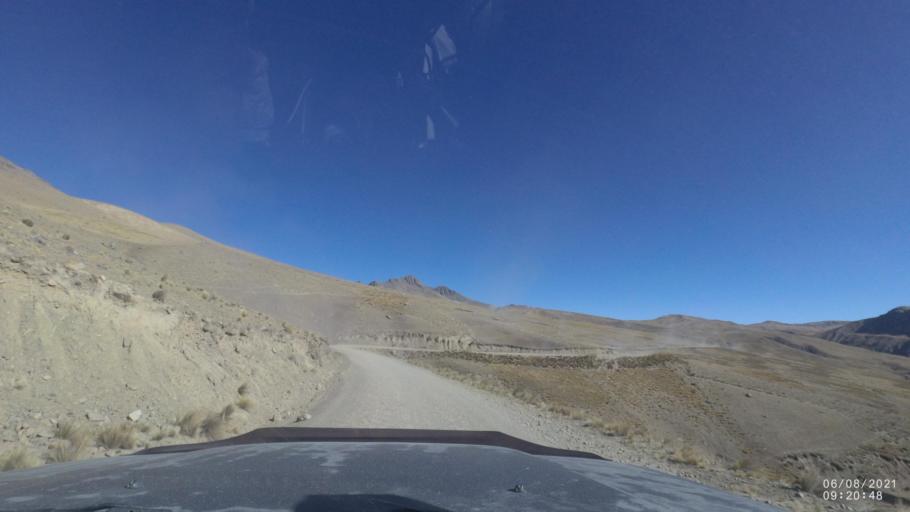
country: BO
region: Cochabamba
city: Colchani
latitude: -17.0239
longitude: -66.5419
